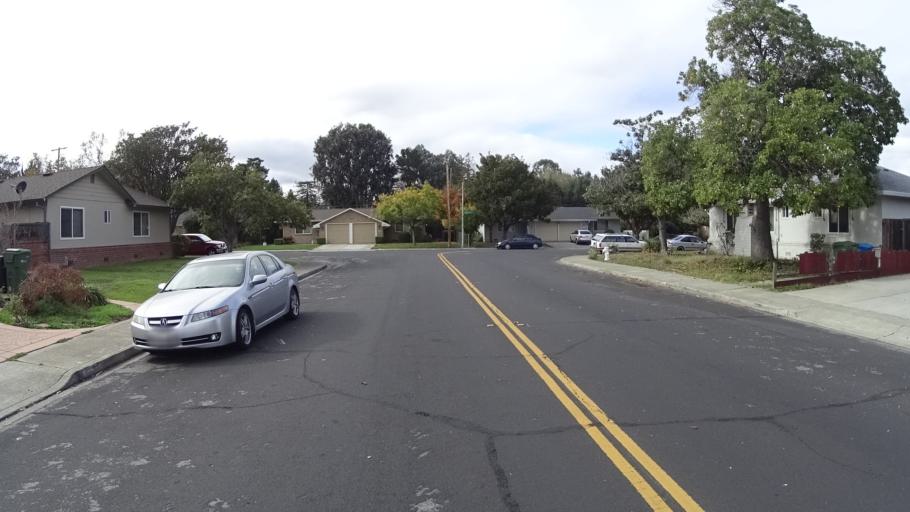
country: US
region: California
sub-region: Santa Clara County
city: Cupertino
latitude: 37.3247
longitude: -121.9947
